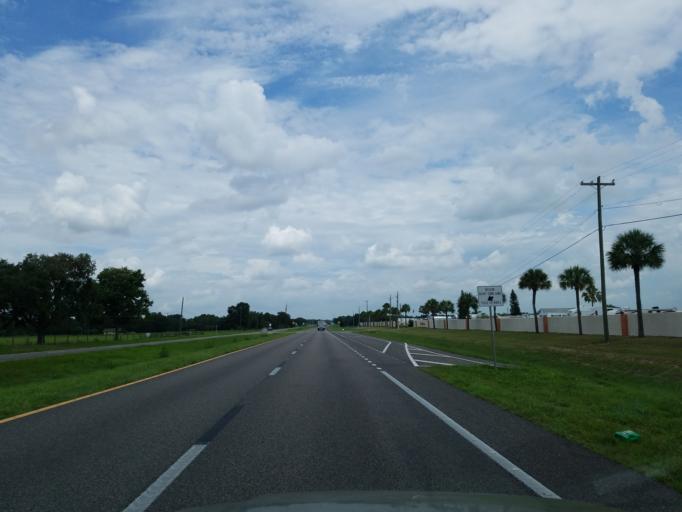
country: US
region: Florida
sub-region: Polk County
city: Wahneta
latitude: 27.9162
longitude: -81.7376
